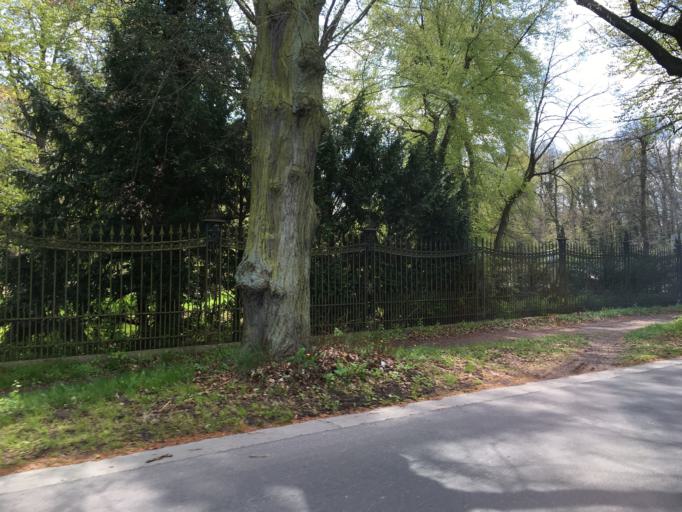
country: DE
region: Brandenburg
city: Potsdam
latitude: 52.4061
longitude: 13.0145
